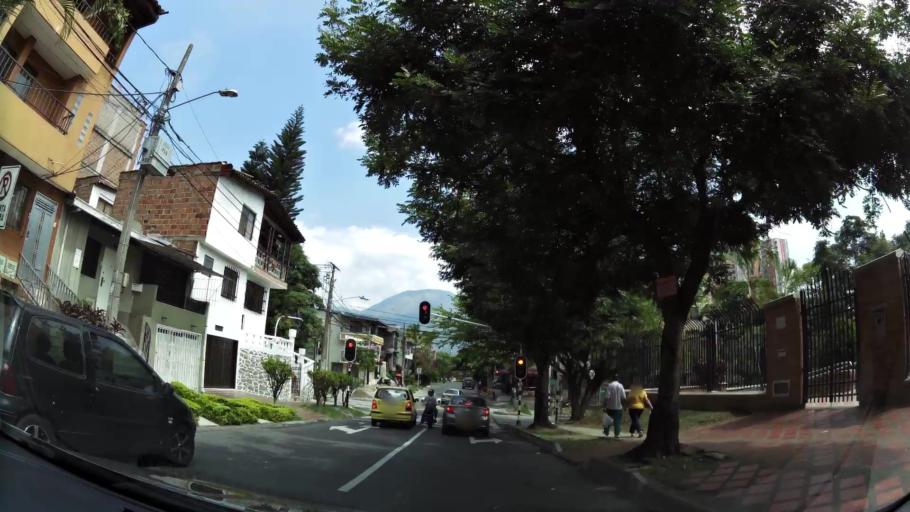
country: CO
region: Antioquia
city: Bello
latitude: 6.3165
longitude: -75.5594
